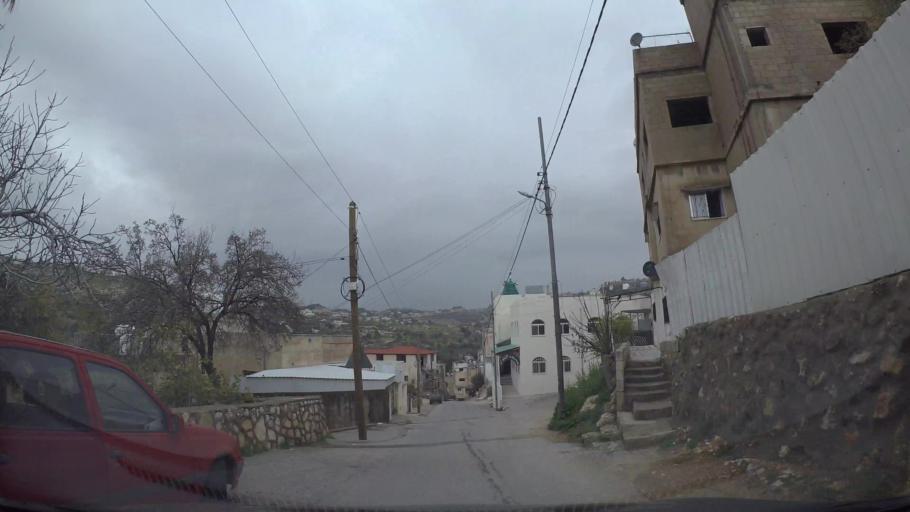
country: JO
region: Amman
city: Wadi as Sir
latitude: 31.9482
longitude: 35.8152
